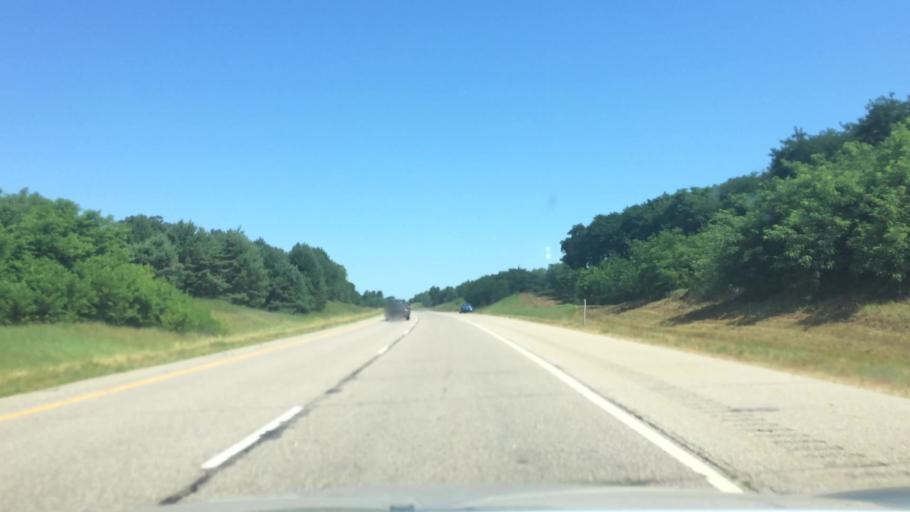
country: US
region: Wisconsin
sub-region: Marquette County
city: Westfield
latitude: 44.0838
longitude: -89.5319
